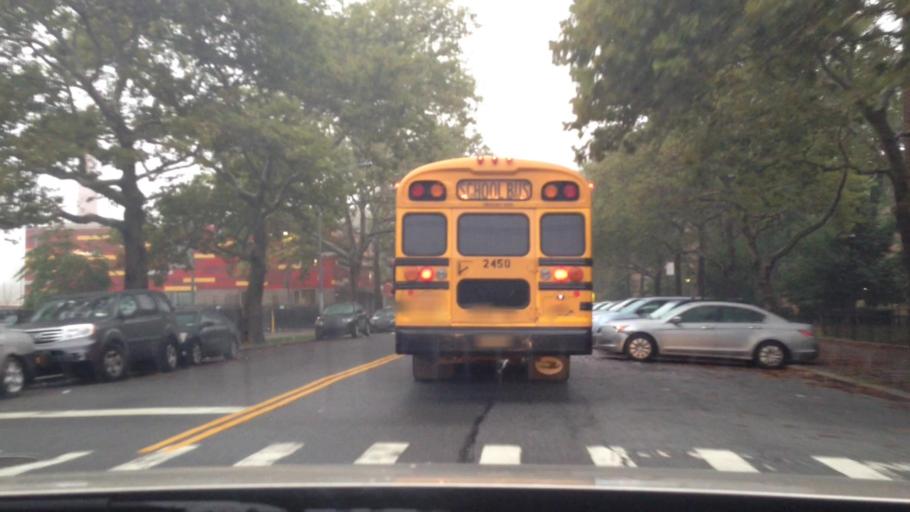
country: US
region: New York
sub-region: Kings County
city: East New York
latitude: 40.6583
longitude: -73.8819
